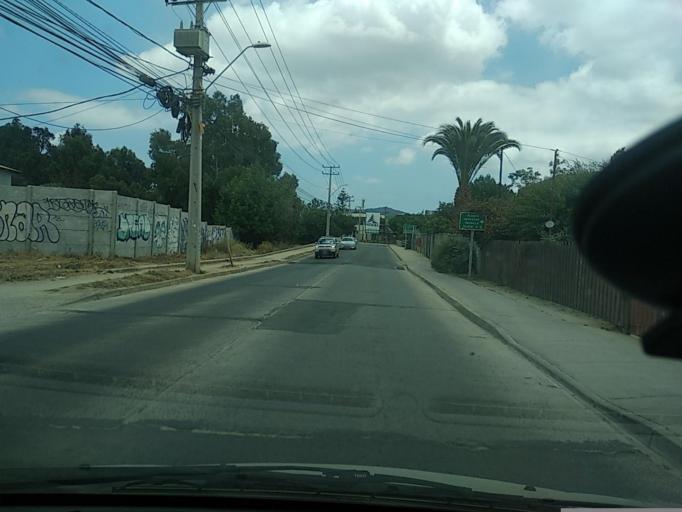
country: CL
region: Valparaiso
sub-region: Provincia de Marga Marga
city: Quilpue
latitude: -33.0418
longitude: -71.4112
